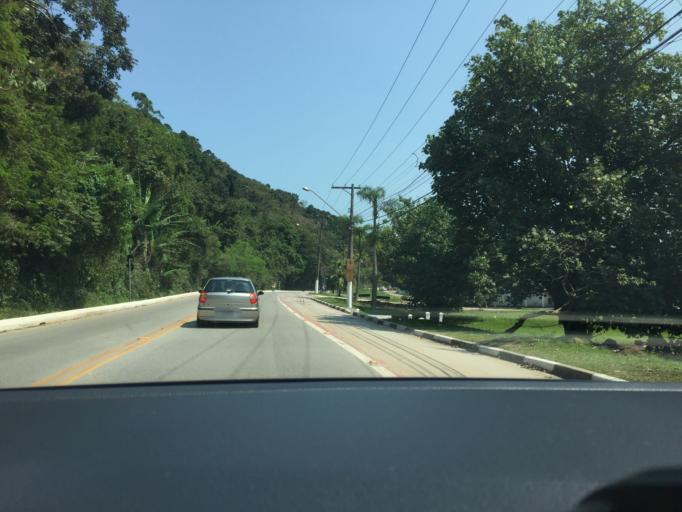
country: BR
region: Sao Paulo
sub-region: Guaruja
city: Guaruja
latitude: -23.9823
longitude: -46.1976
